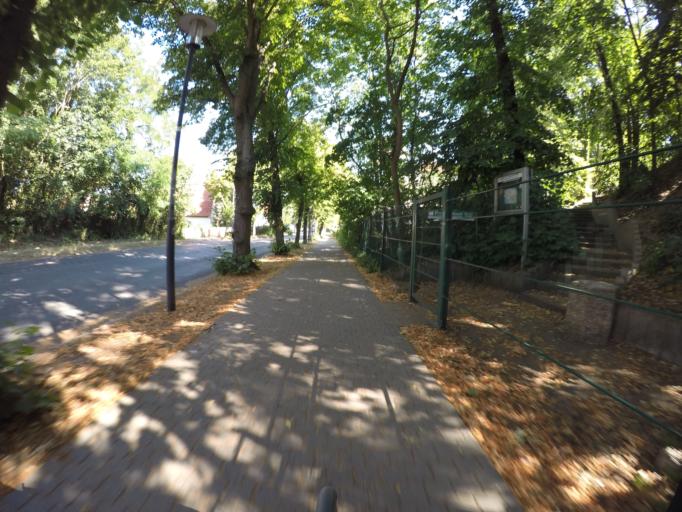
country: DE
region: Brandenburg
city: Woltersdorf
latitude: 52.4463
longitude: 13.7620
